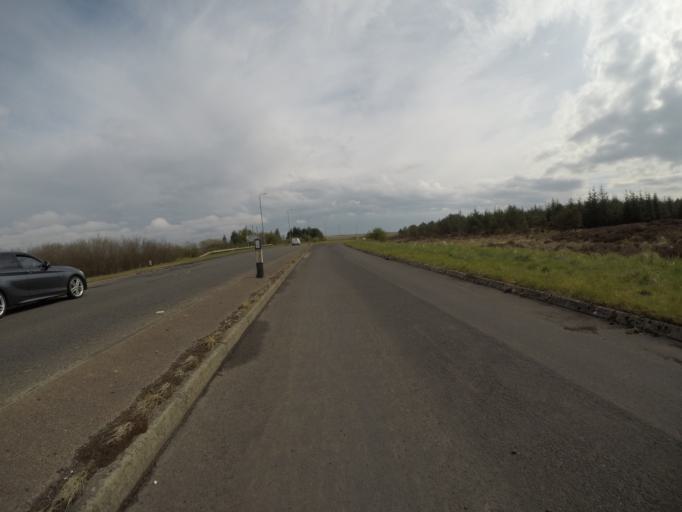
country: GB
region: Scotland
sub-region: East Renfrewshire
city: Neilston
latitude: 55.6977
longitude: -4.3939
